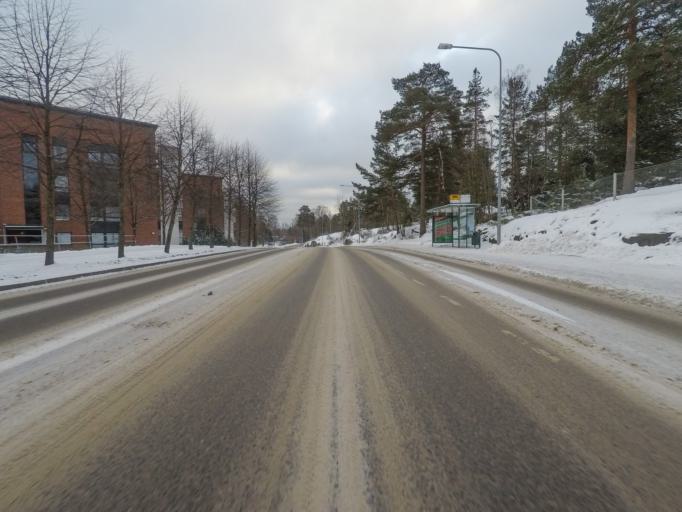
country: FI
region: Uusimaa
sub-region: Helsinki
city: Vantaa
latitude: 60.2183
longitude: 25.1465
